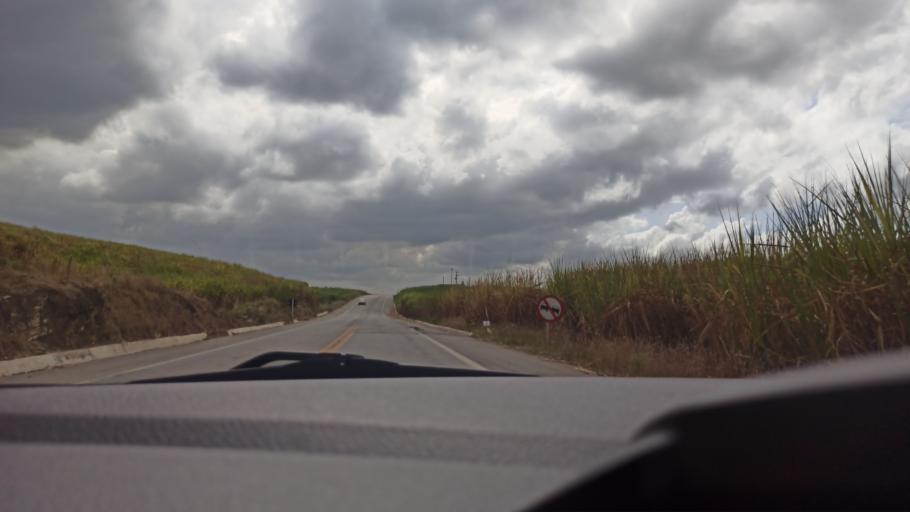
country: BR
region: Pernambuco
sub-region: Timbauba
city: Timbauba
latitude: -7.5446
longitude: -35.2710
